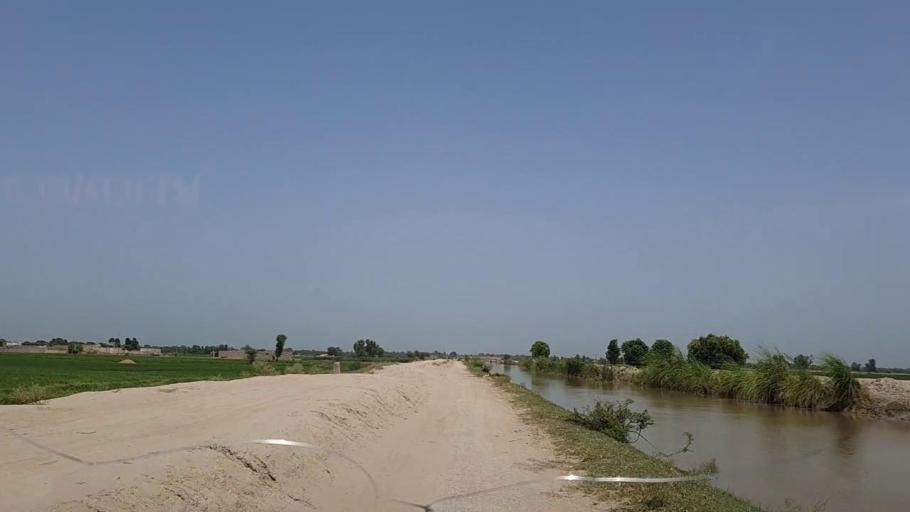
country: PK
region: Sindh
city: Tharu Shah
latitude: 26.9867
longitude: 68.0831
